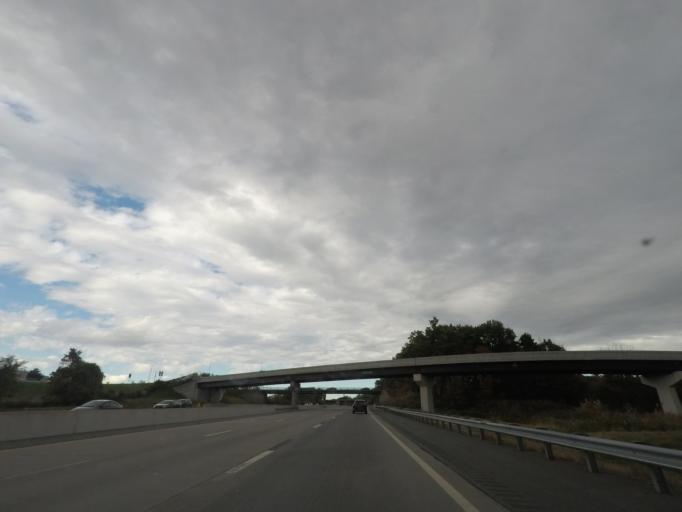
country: US
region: New York
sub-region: Albany County
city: McKownville
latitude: 42.6860
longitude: -73.8448
